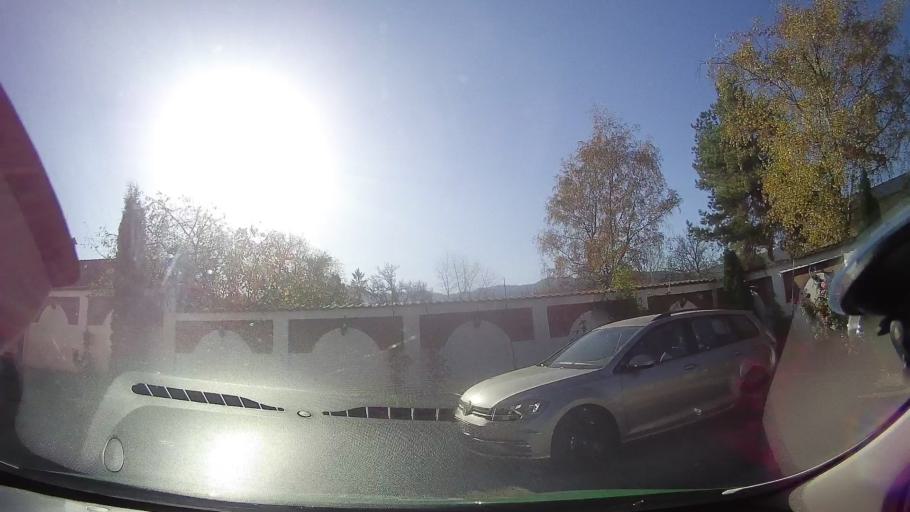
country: RO
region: Brasov
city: Brasov
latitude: 45.6617
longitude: 25.5811
